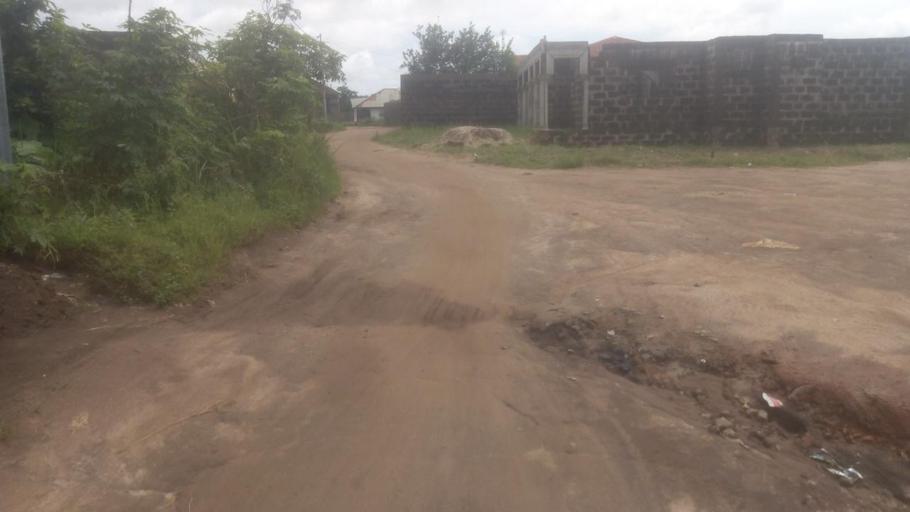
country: SL
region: Northern Province
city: Masoyila
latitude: 8.5975
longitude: -13.1873
